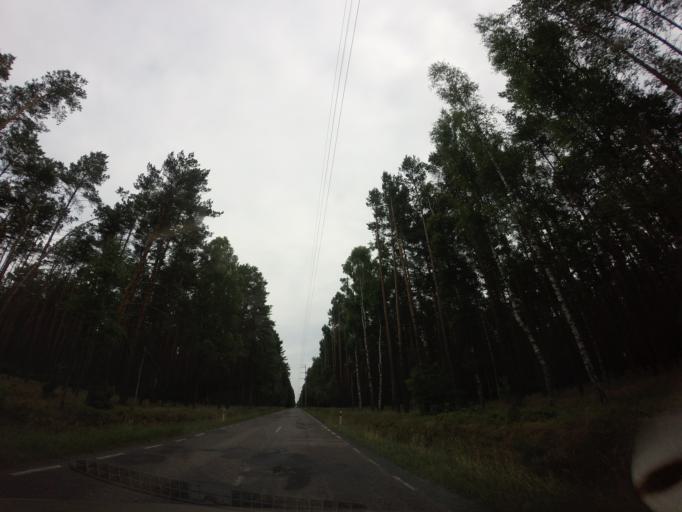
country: PL
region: West Pomeranian Voivodeship
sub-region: Powiat drawski
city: Czaplinek
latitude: 53.4658
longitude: 16.2207
